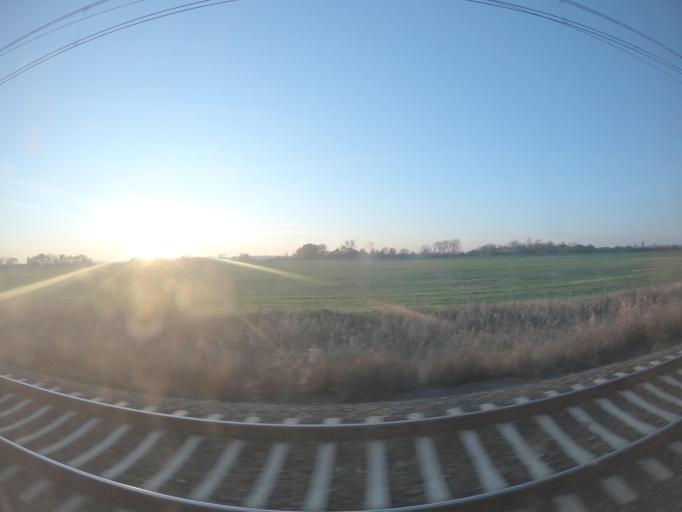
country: PL
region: Lubusz
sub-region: Powiat gorzowski
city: Kostrzyn nad Odra
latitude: 52.5411
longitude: 14.6509
